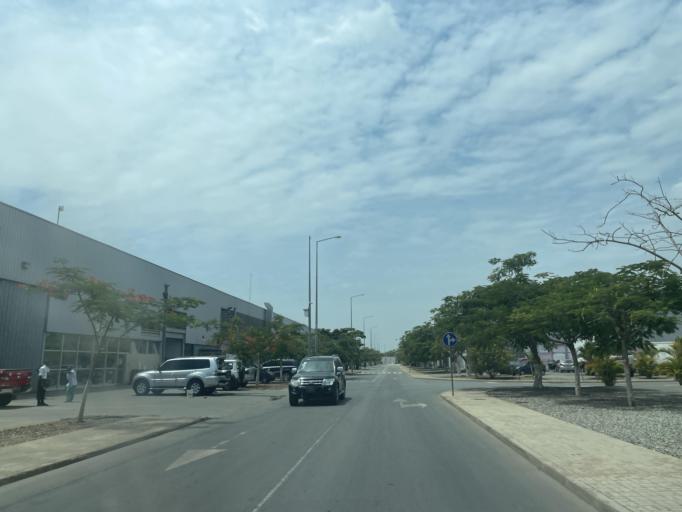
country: AO
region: Luanda
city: Luanda
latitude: -8.9612
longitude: 13.3898
